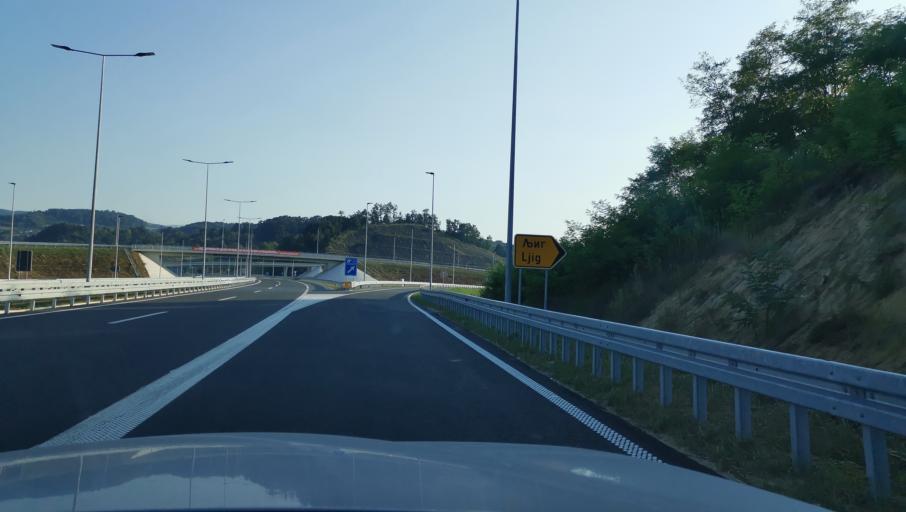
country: RS
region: Central Serbia
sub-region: Kolubarski Okrug
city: Ljig
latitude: 44.2346
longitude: 20.2551
